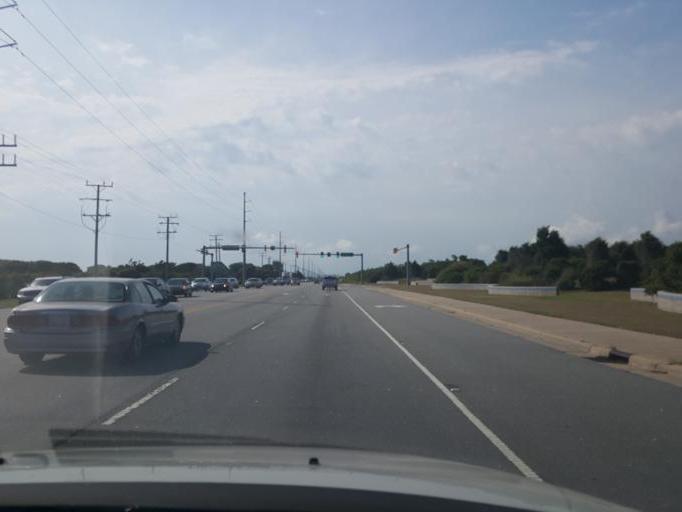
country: US
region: North Carolina
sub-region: Dare County
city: Kill Devil Hills
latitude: 36.0213
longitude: -75.6656
